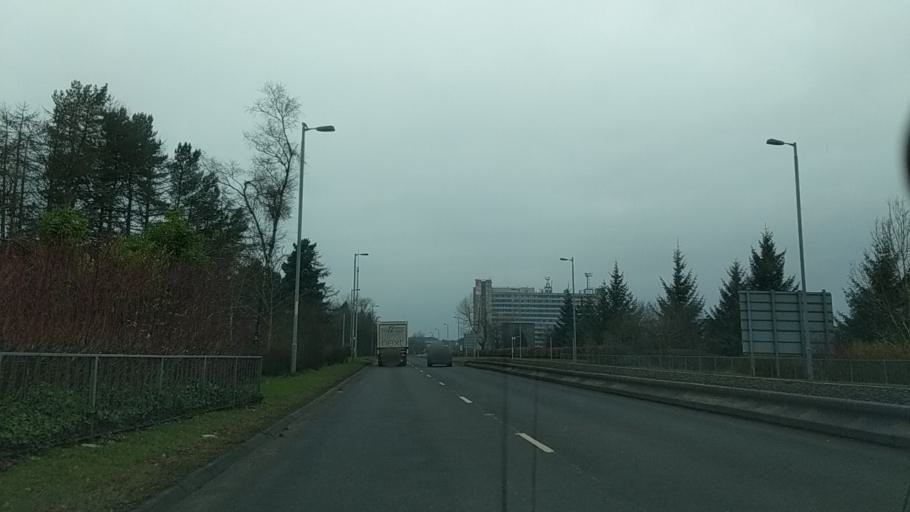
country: GB
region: Scotland
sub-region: South Lanarkshire
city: East Kilbride
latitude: 55.7584
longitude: -4.1726
